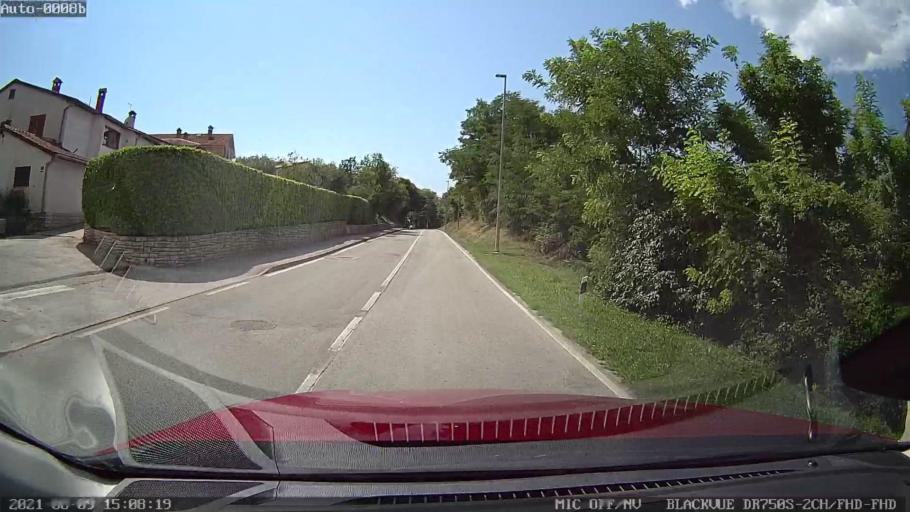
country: HR
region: Istarska
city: Pazin
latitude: 45.2448
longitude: 13.9552
